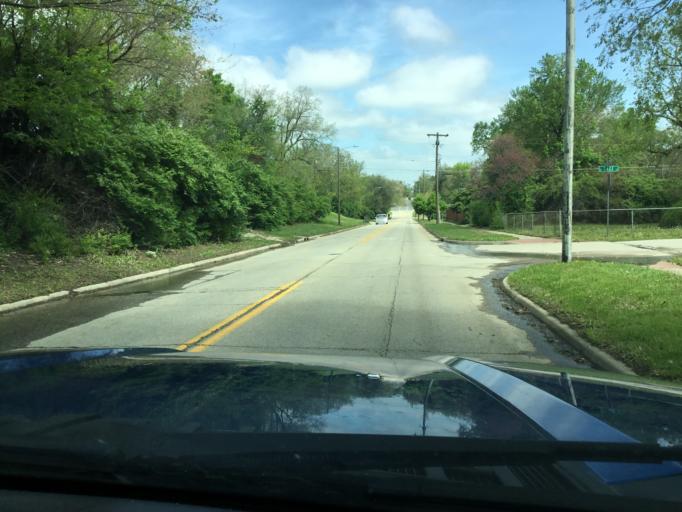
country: US
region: Kansas
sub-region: Shawnee County
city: Topeka
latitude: 39.0268
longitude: -95.6606
